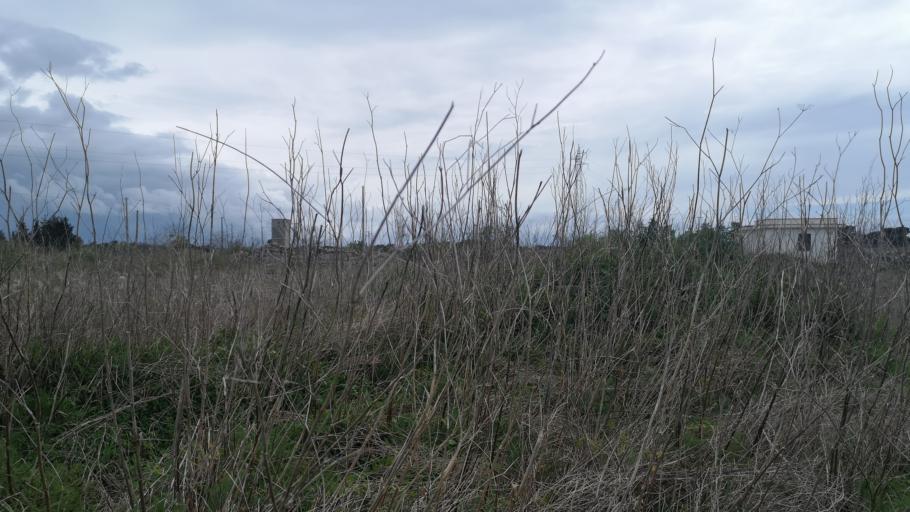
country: IT
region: Apulia
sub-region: Provincia di Lecce
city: Ortelle
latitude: 40.0286
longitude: 18.3794
